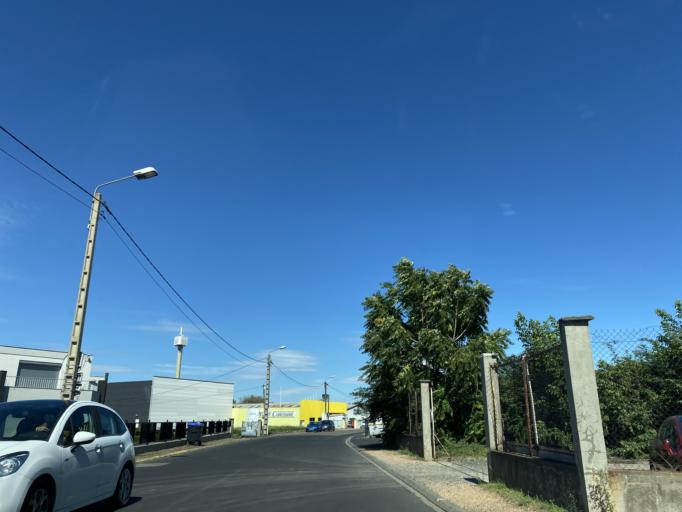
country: FR
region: Auvergne
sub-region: Departement du Puy-de-Dome
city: Perignat-les-Sarlieve
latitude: 45.7543
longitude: 3.1331
